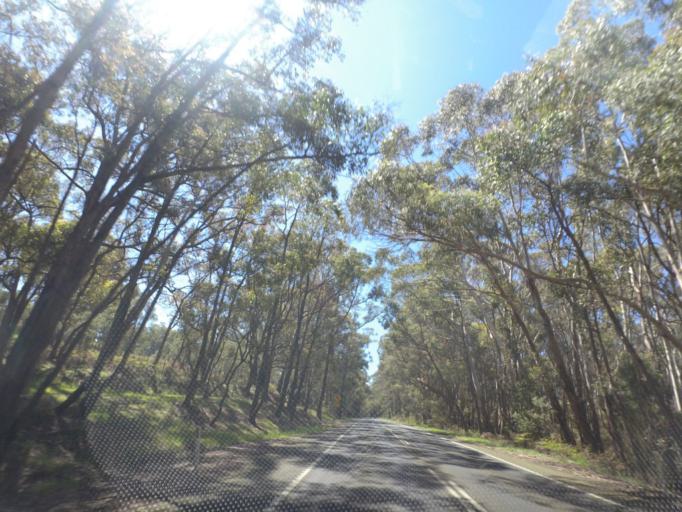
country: AU
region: Victoria
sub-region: Hume
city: Sunbury
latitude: -37.2279
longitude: 144.7414
